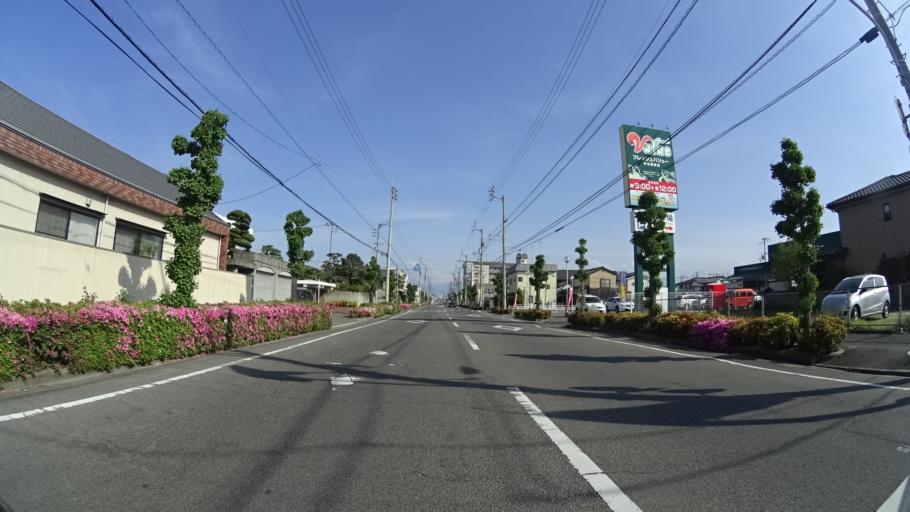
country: JP
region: Ehime
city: Saijo
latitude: 34.0624
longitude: 133.0101
